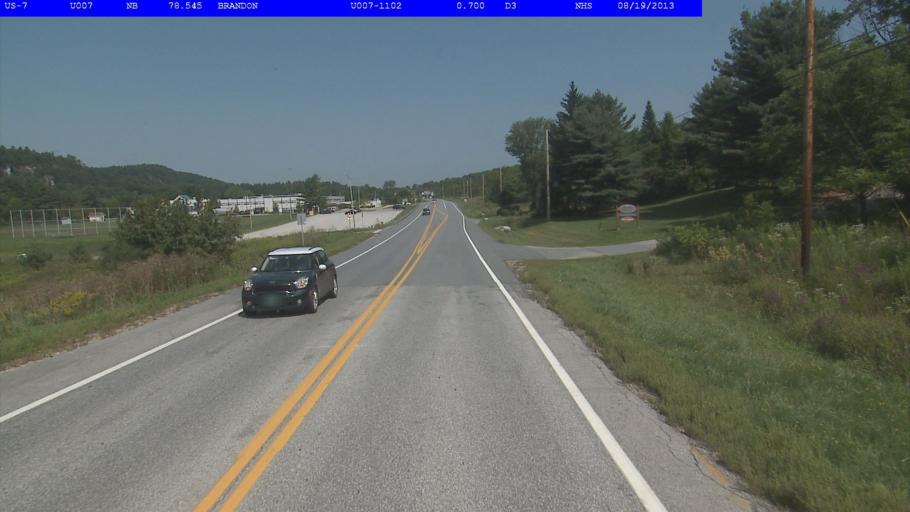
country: US
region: Vermont
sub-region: Rutland County
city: Brandon
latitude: 43.7644
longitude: -73.0501
